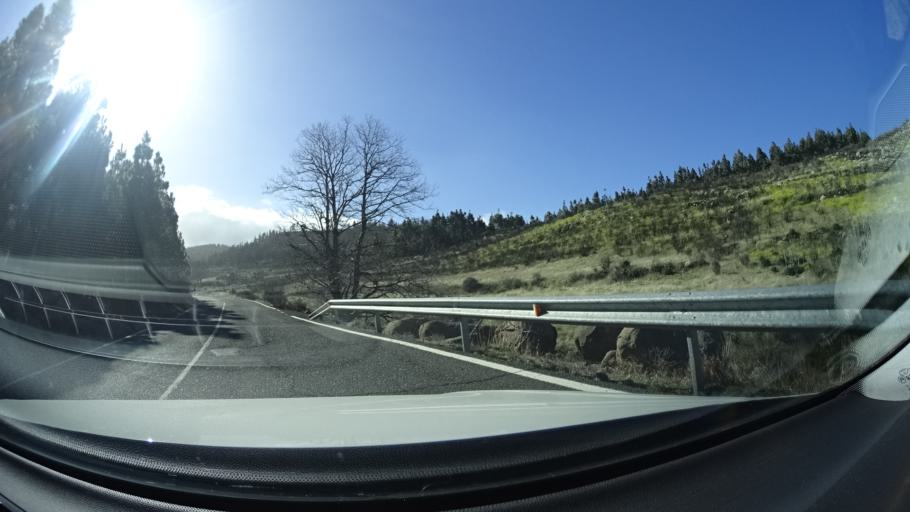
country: ES
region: Canary Islands
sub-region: Provincia de Las Palmas
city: San Bartolome
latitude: 27.9653
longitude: -15.5576
